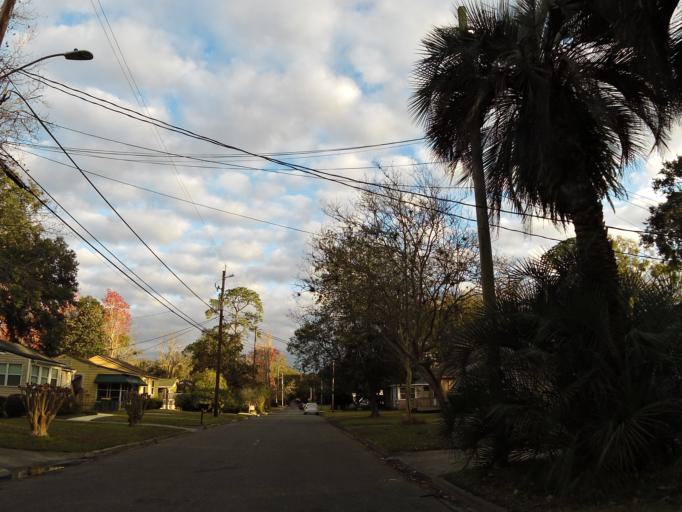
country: US
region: Florida
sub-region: Duval County
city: Jacksonville
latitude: 30.3021
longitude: -81.7144
